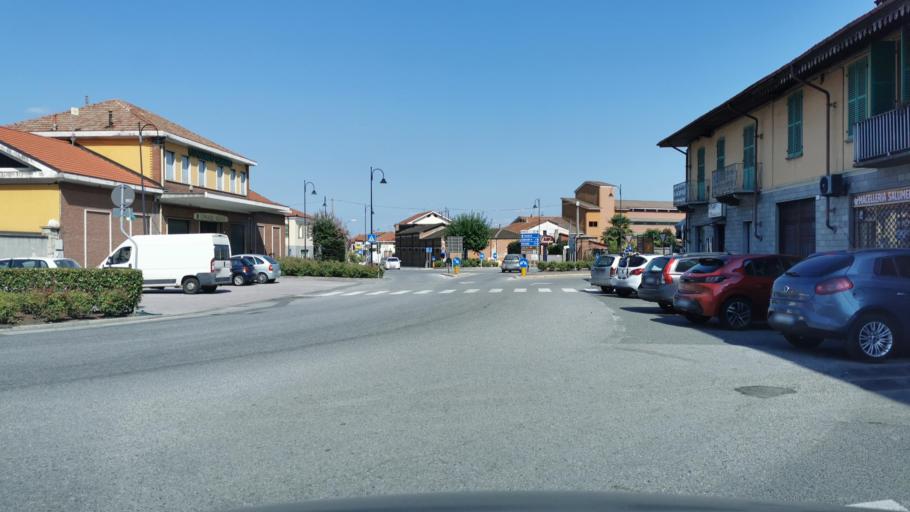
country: IT
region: Piedmont
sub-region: Provincia di Cuneo
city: Revello
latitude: 44.6567
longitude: 7.3920
